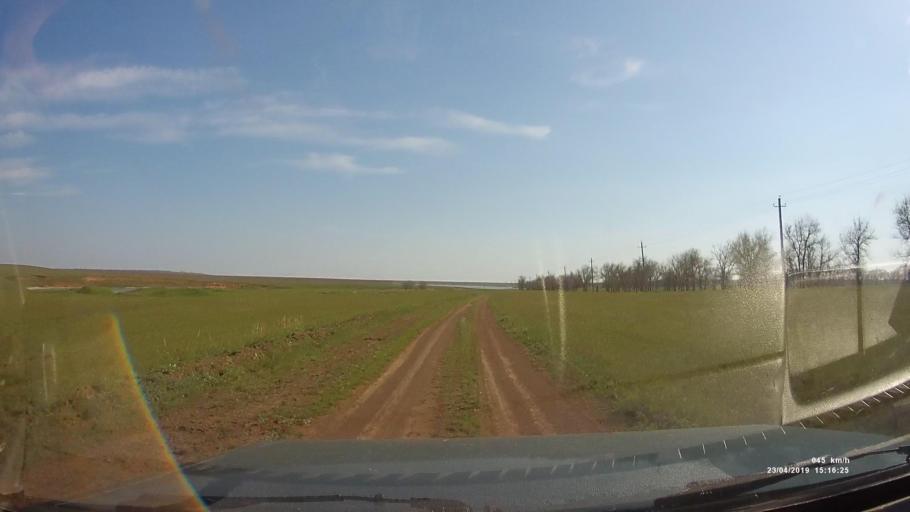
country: RU
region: Rostov
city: Remontnoye
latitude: 46.5336
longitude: 42.9699
